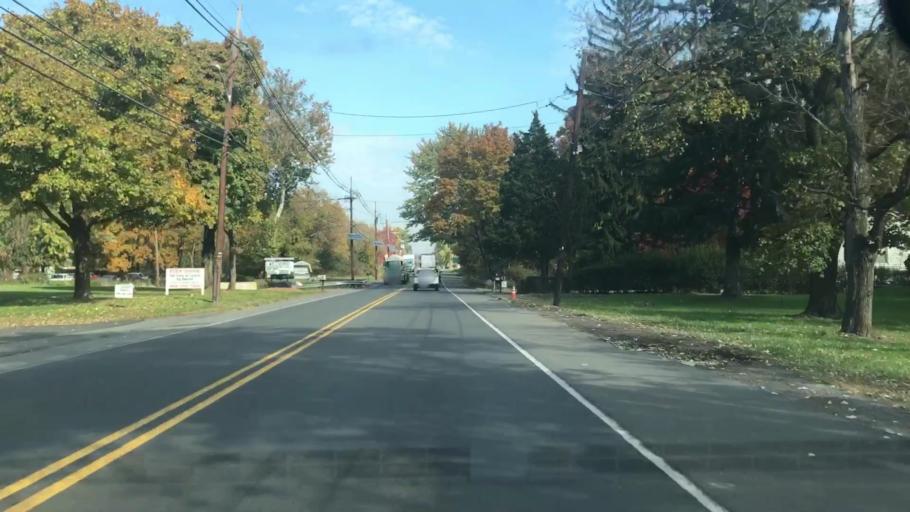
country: US
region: New Jersey
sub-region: Somerset County
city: Weston
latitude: 40.5305
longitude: -74.6241
